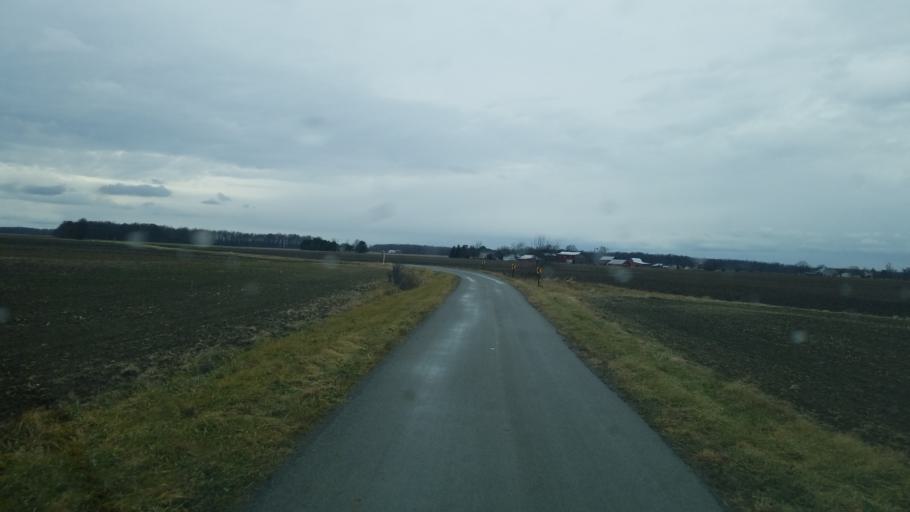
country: US
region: Ohio
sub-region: Hardin County
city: Forest
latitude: 40.7517
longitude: -83.4137
